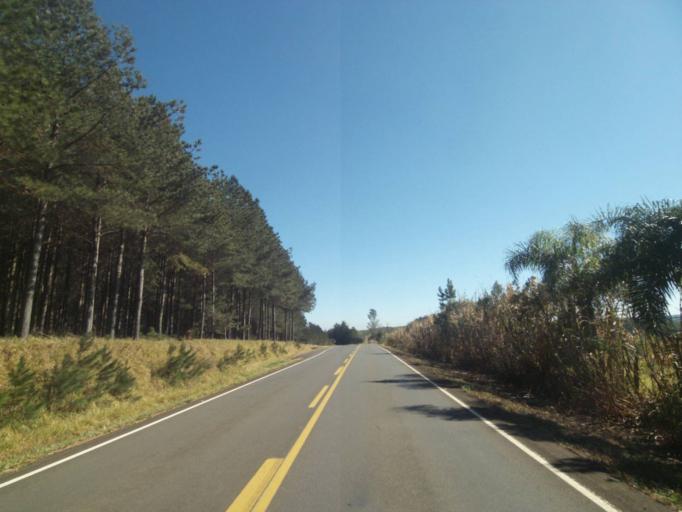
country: BR
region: Parana
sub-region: Telemaco Borba
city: Telemaco Borba
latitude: -24.4332
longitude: -50.5567
